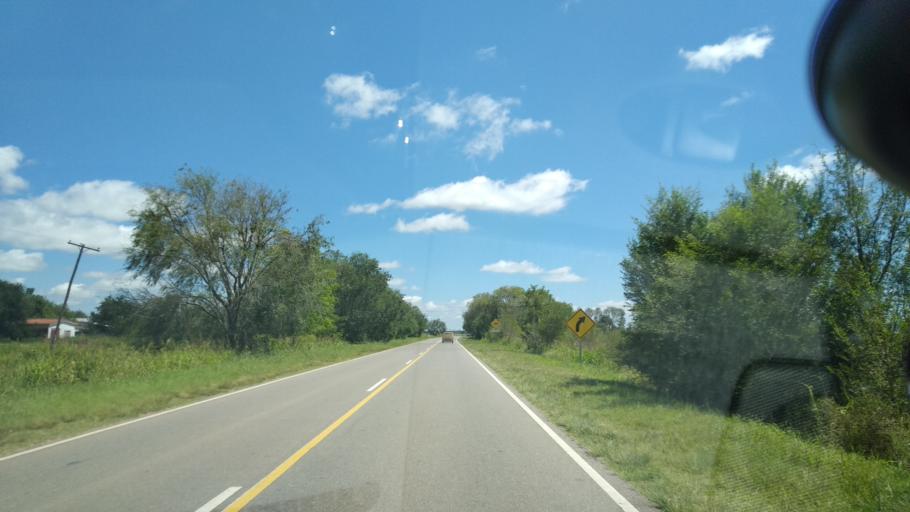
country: AR
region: Cordoba
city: Villa Cura Brochero
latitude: -31.5852
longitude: -65.1116
